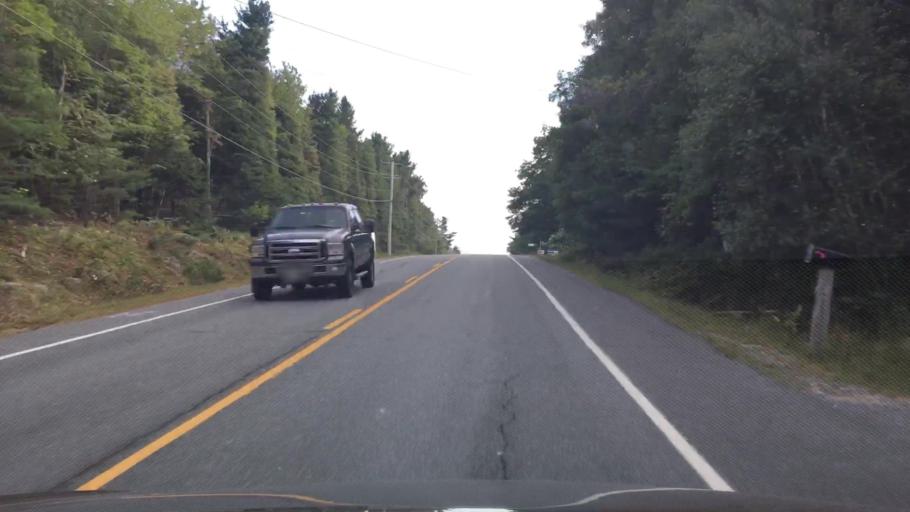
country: US
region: Maine
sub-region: Hancock County
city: Surry
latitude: 44.4804
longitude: -68.5183
